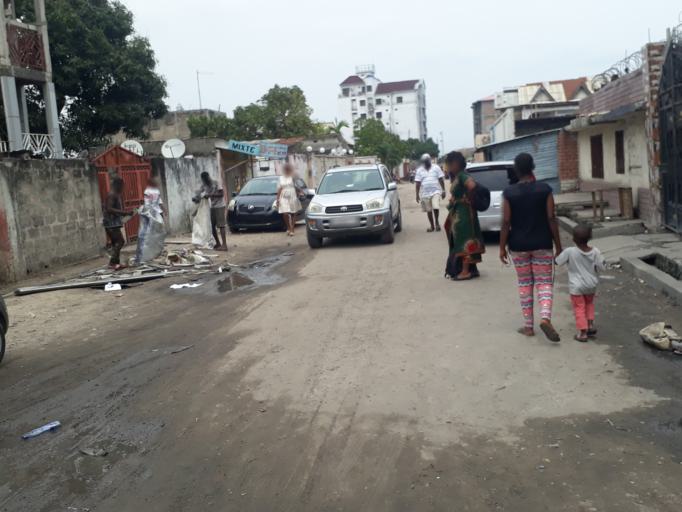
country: CD
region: Kinshasa
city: Kinshasa
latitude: -4.3094
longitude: 15.3197
